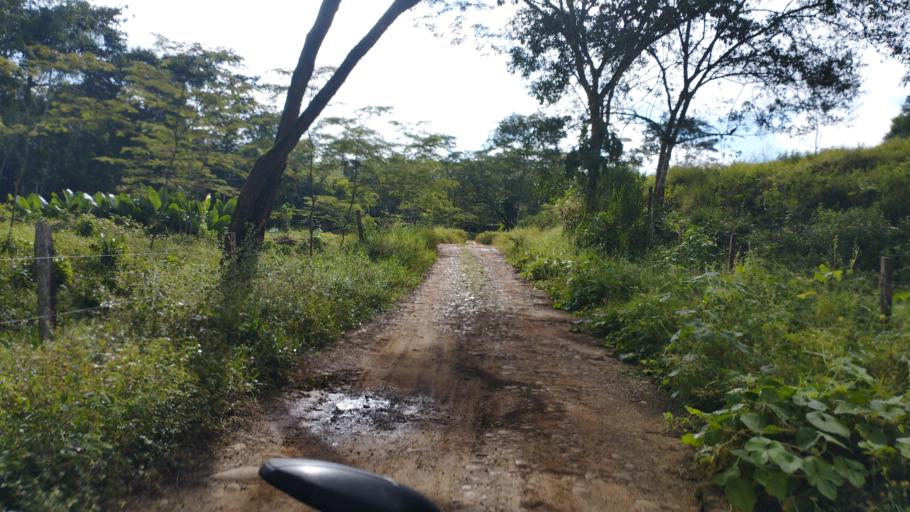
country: CO
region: Casanare
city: Sabanalarga
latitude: 4.7589
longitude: -73.0720
